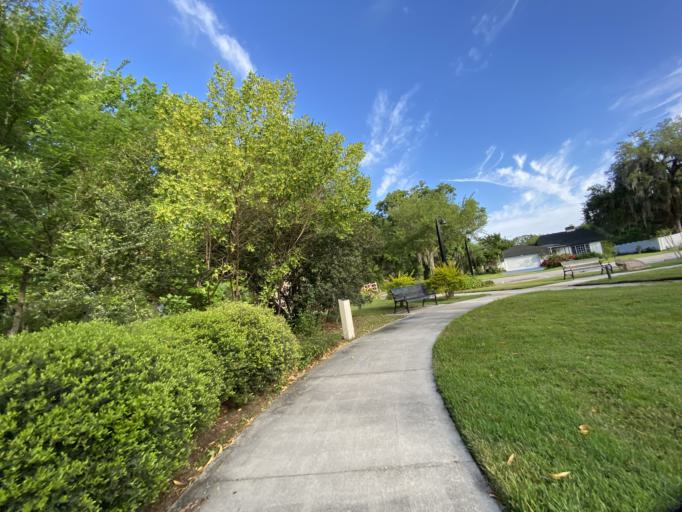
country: US
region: Florida
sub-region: Volusia County
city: South Daytona
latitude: 29.1723
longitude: -81.0137
